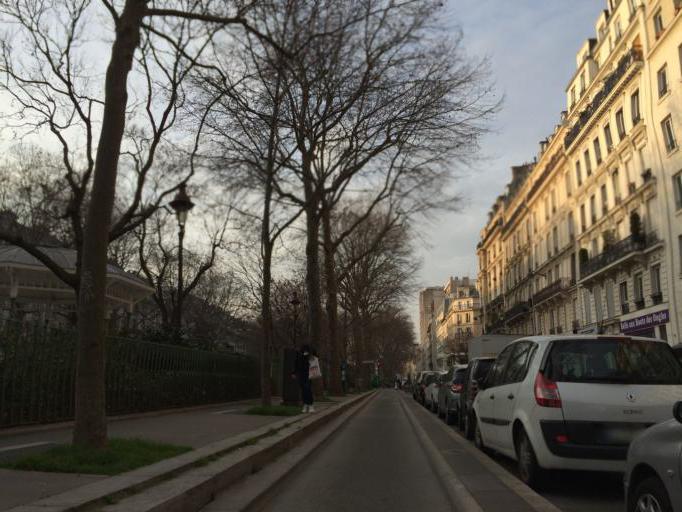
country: FR
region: Ile-de-France
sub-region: Paris
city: Paris
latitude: 48.8678
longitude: 2.3684
